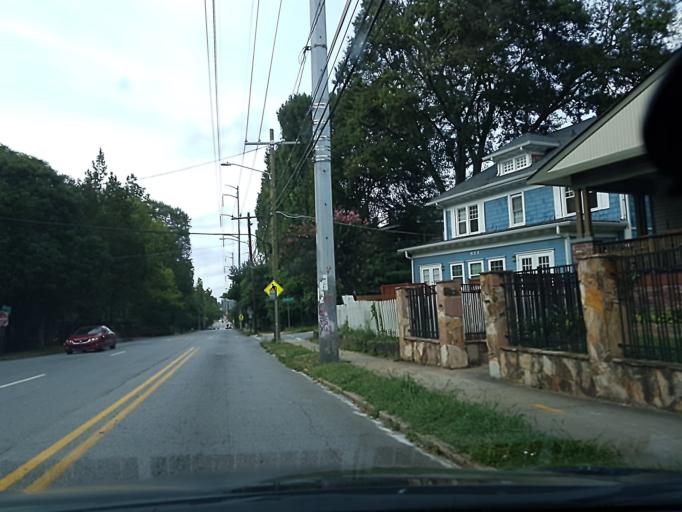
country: US
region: Georgia
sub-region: Fulton County
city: Atlanta
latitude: 33.7765
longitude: -84.3703
